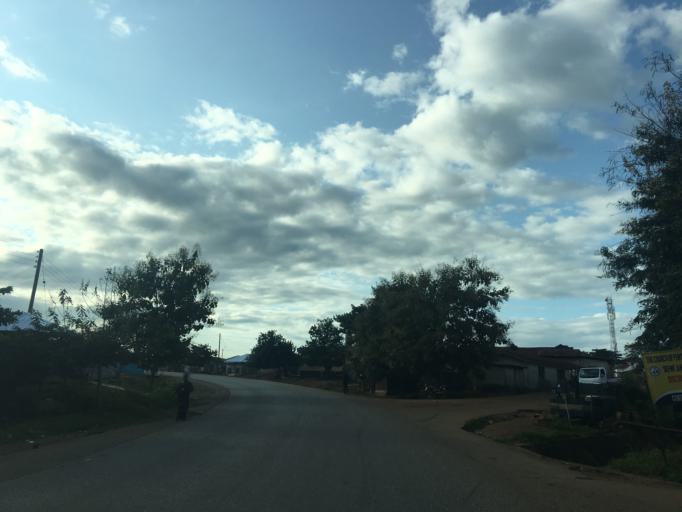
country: GH
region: Western
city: Bibiani
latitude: 6.3283
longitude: -2.2500
